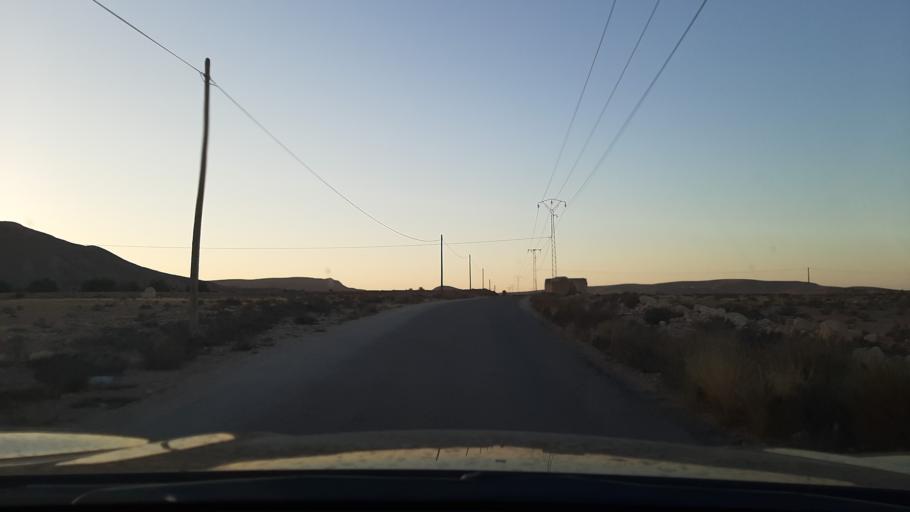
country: TN
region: Qabis
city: Matmata
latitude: 33.5496
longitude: 10.1890
